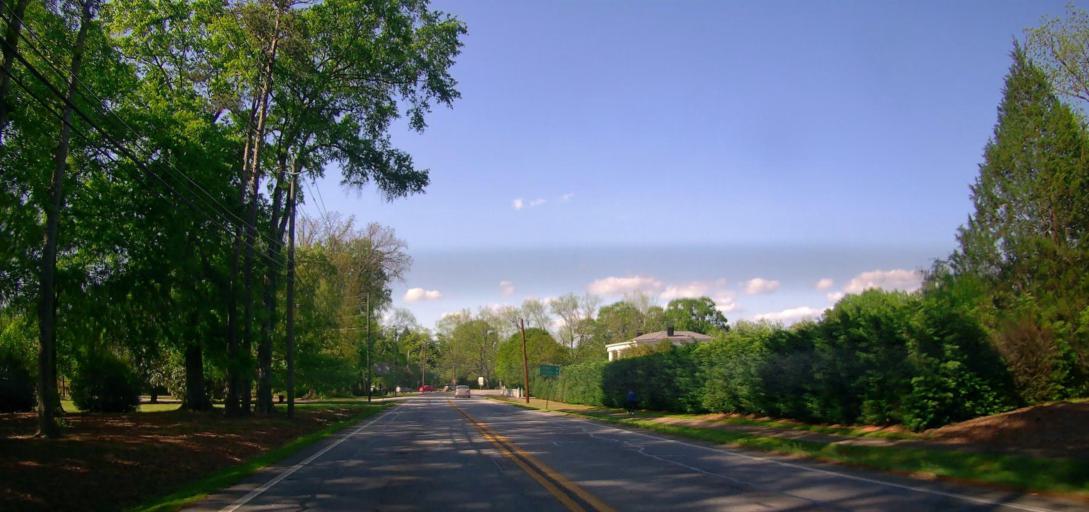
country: US
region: Georgia
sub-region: Morgan County
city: Madison
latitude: 33.5850
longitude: -83.4776
